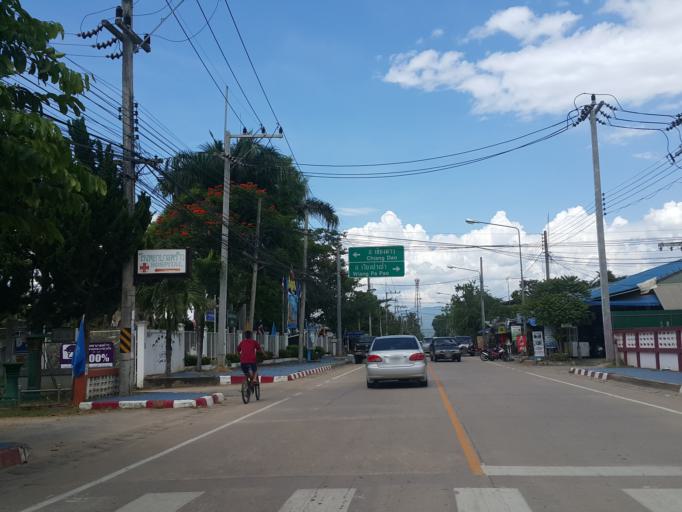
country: TH
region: Chiang Mai
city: Phrao
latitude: 19.3669
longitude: 99.2008
